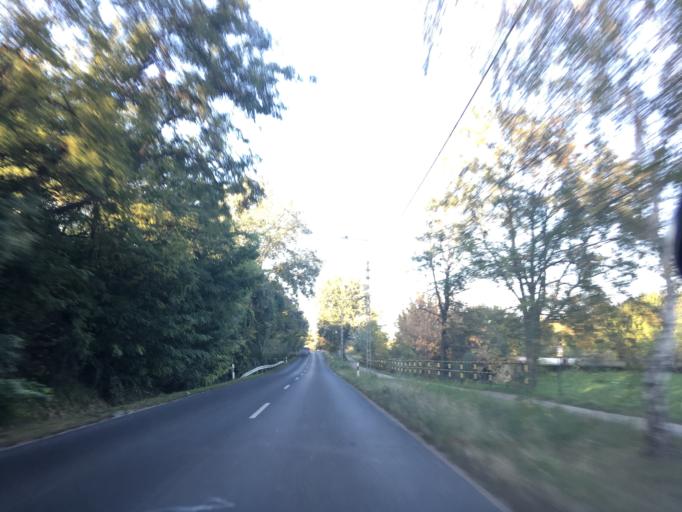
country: HU
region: Pest
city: Szazhalombatta
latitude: 47.3106
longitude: 18.8978
